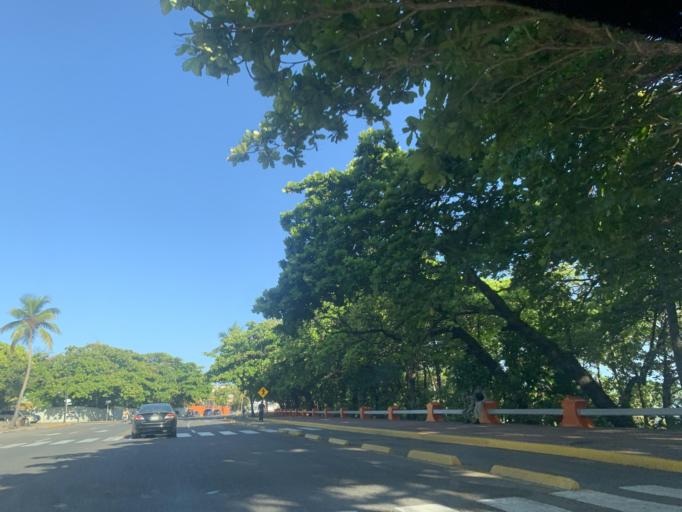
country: DO
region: Puerto Plata
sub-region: Puerto Plata
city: Puerto Plata
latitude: 19.7980
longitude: -70.6865
